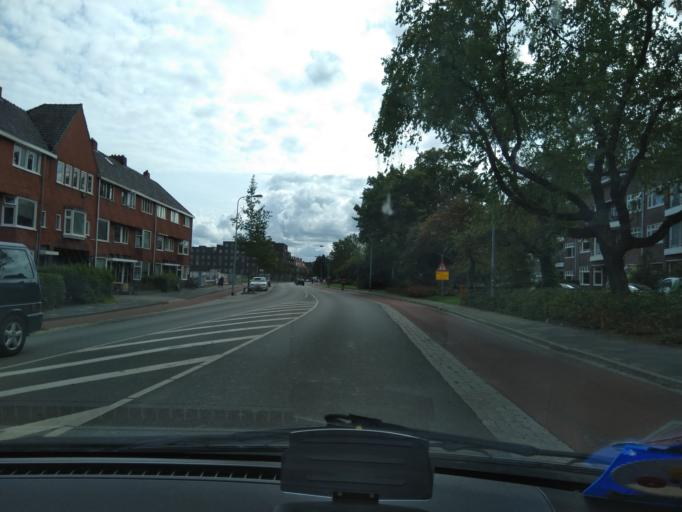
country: NL
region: Groningen
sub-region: Gemeente Groningen
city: Groningen
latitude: 53.2099
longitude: 6.5567
